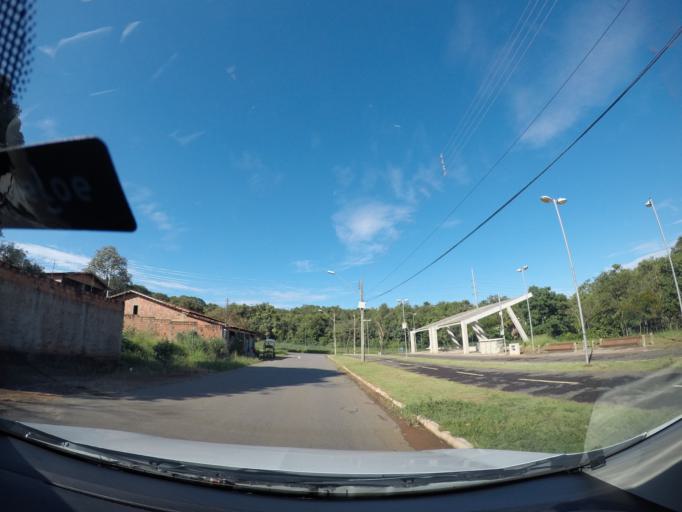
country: BR
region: Goias
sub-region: Goiania
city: Goiania
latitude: -16.7390
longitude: -49.3180
